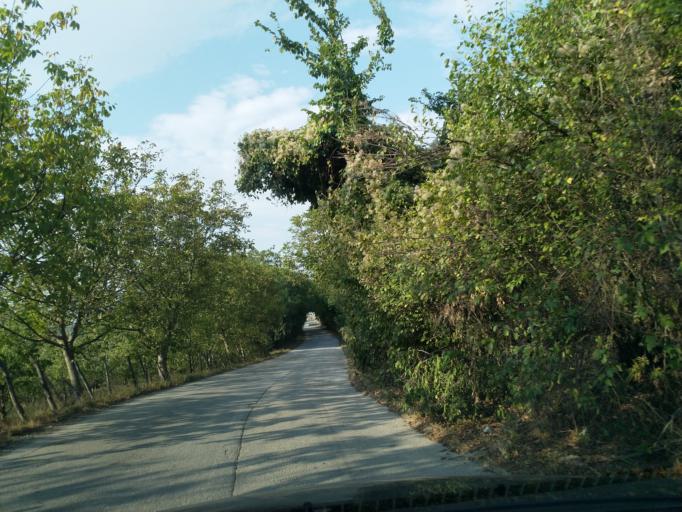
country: RS
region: Central Serbia
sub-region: Pomoravski Okrug
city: Paracin
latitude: 43.8463
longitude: 21.5271
